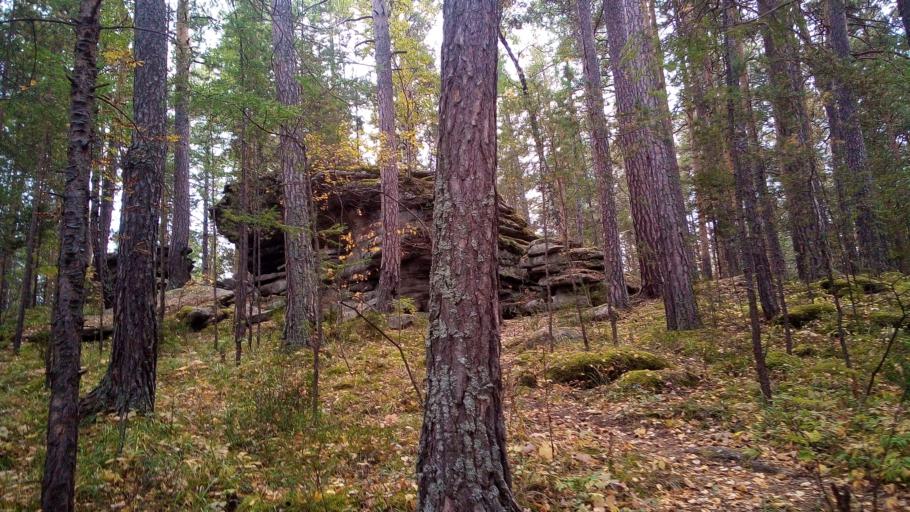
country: RU
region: Chelyabinsk
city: Turgoyak
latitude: 55.1753
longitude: 60.0208
